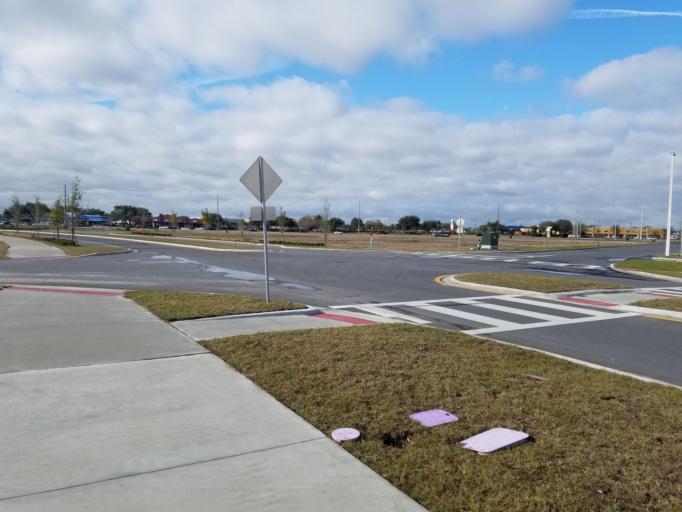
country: US
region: Florida
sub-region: Osceola County
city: Celebration
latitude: 28.3449
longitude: -81.4821
